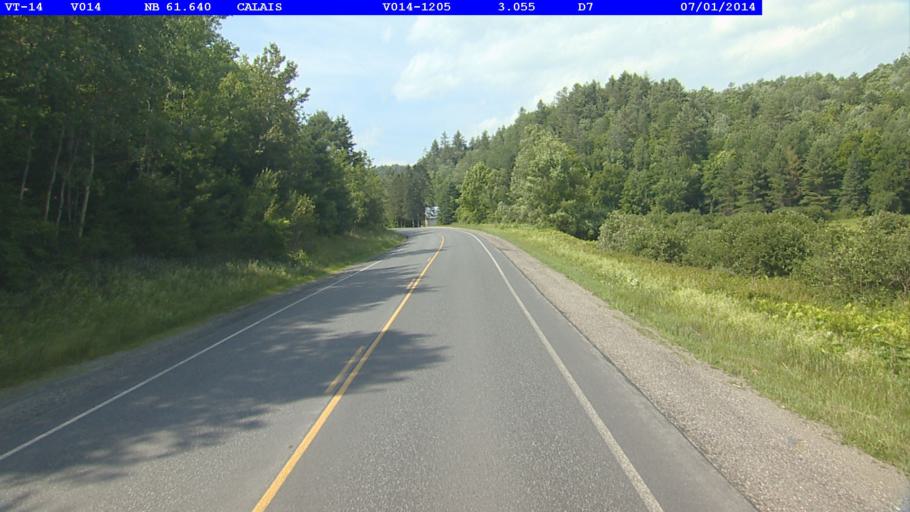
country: US
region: Vermont
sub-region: Washington County
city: Montpelier
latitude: 44.3502
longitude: -72.4422
